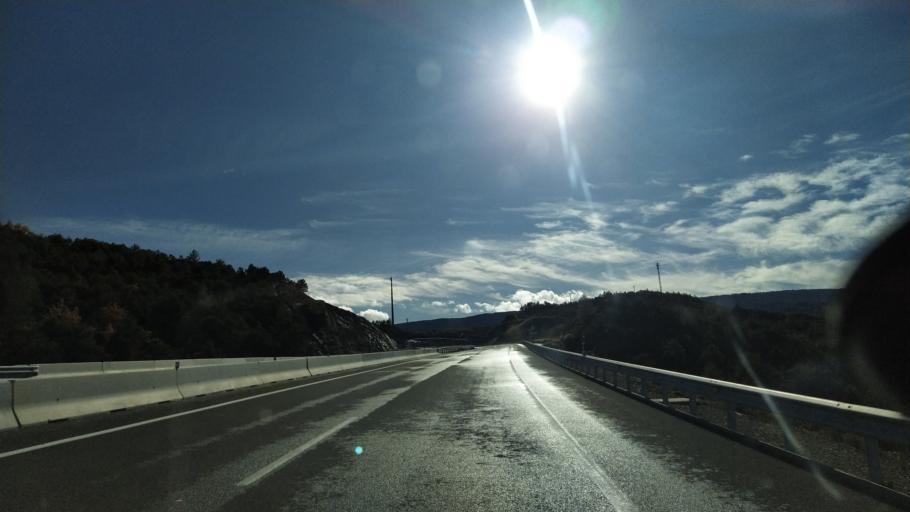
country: ES
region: Aragon
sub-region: Provincia de Huesca
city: Arguis
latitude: 42.4000
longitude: -0.3734
